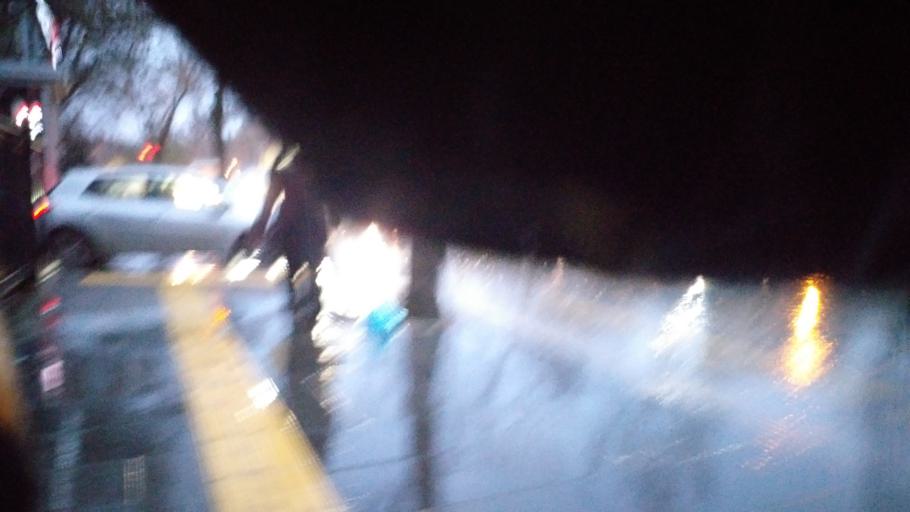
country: TR
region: Ankara
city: Ankara
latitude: 39.9344
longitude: 32.8266
